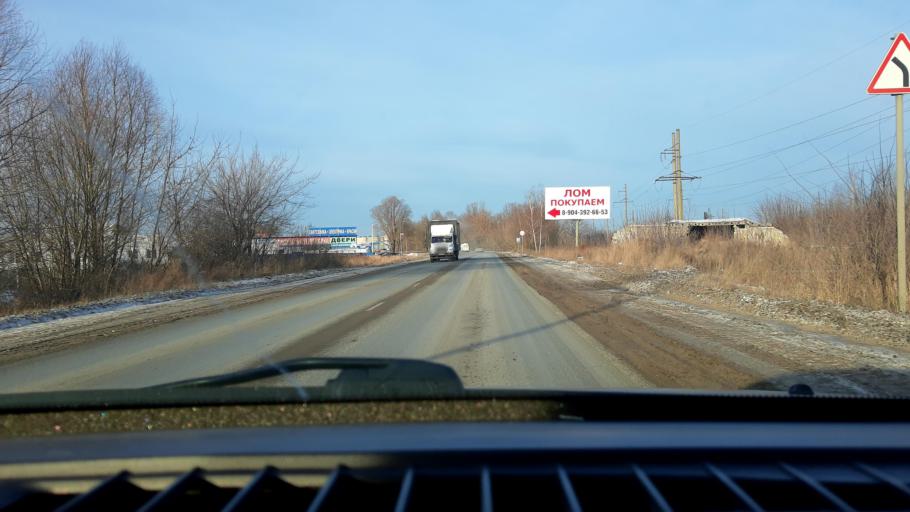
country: RU
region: Nizjnij Novgorod
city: Bor
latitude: 56.3750
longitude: 44.0609
